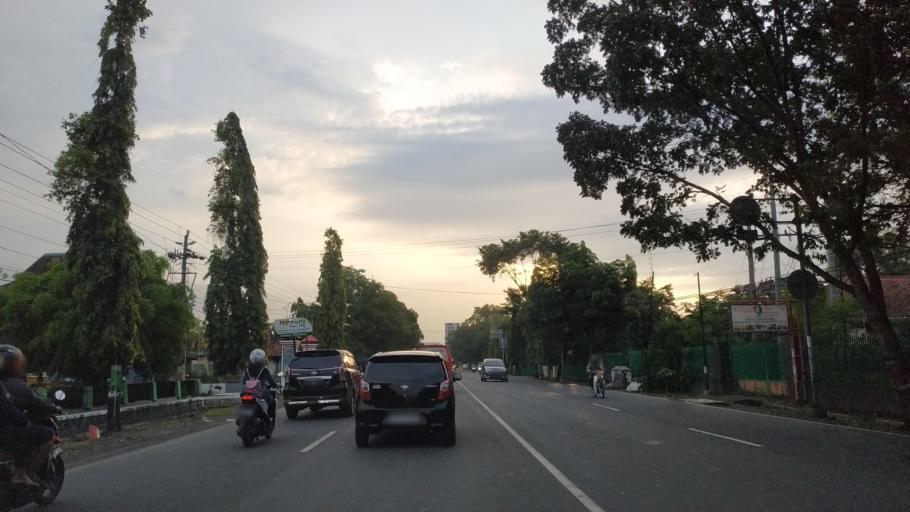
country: ID
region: Central Java
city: Kudus
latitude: -6.8038
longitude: 110.8605
